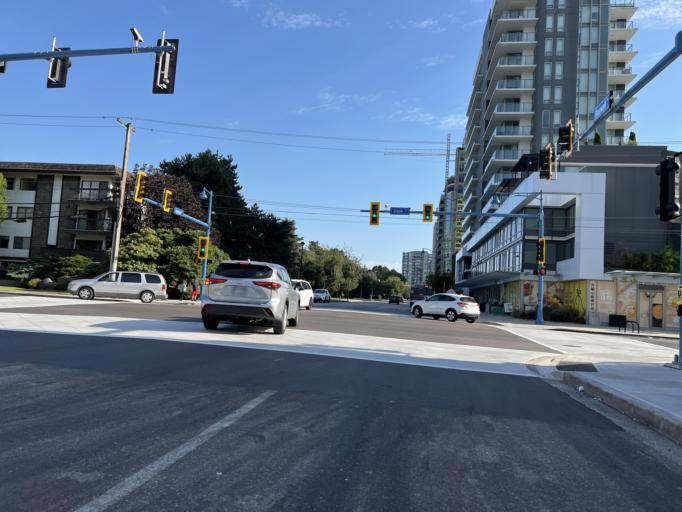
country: CA
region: British Columbia
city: Richmond
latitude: 49.1667
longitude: -123.1338
